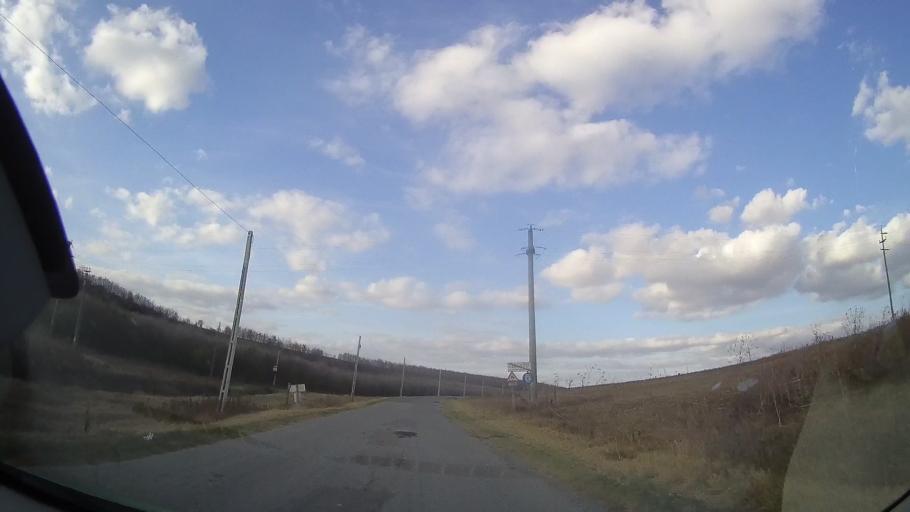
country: RO
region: Constanta
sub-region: Comuna Cerchezu
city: Cerchezu
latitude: 43.8296
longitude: 28.0967
